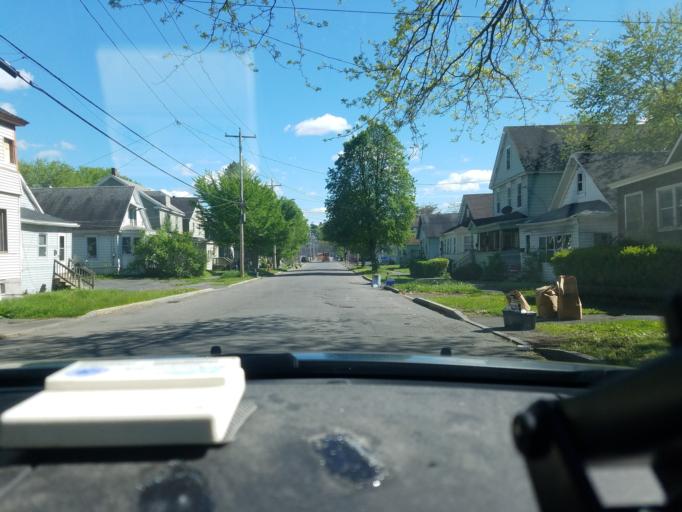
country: US
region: New York
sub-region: Onondaga County
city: Syracuse
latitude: 43.0545
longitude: -76.1304
